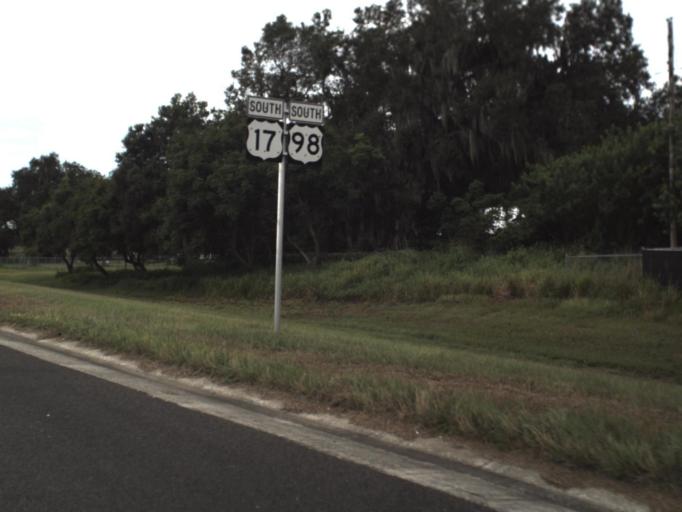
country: US
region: Florida
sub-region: Polk County
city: Fort Meade
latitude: 27.8195
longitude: -81.8217
